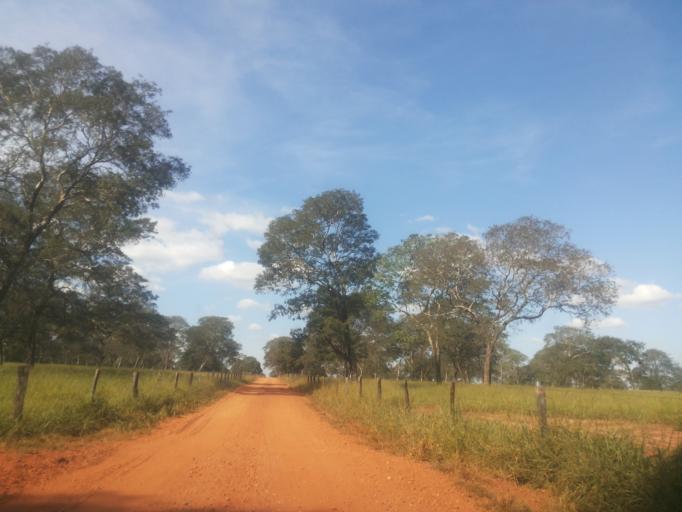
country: BR
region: Minas Gerais
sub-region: Santa Vitoria
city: Santa Vitoria
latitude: -19.0120
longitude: -50.4085
